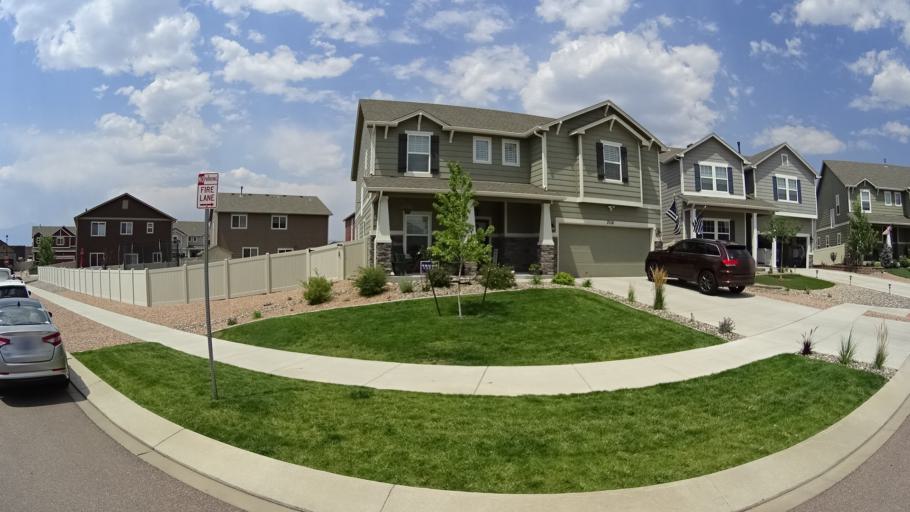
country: US
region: Colorado
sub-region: El Paso County
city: Black Forest
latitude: 38.9529
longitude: -104.6939
